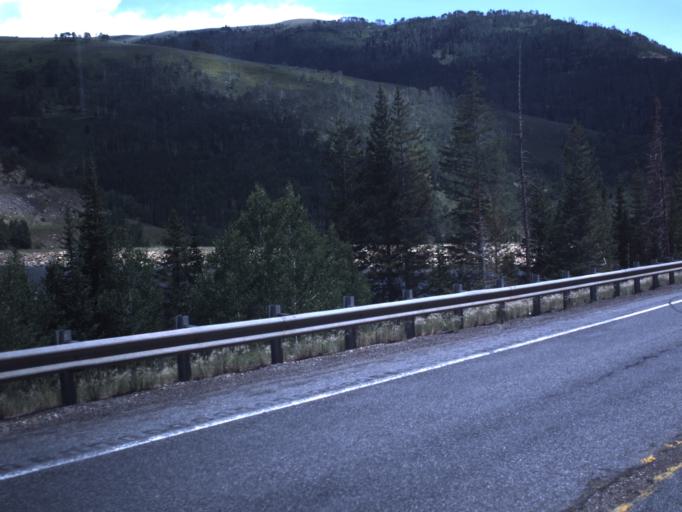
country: US
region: Utah
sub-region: Sanpete County
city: Fairview
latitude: 39.6003
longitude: -111.2151
